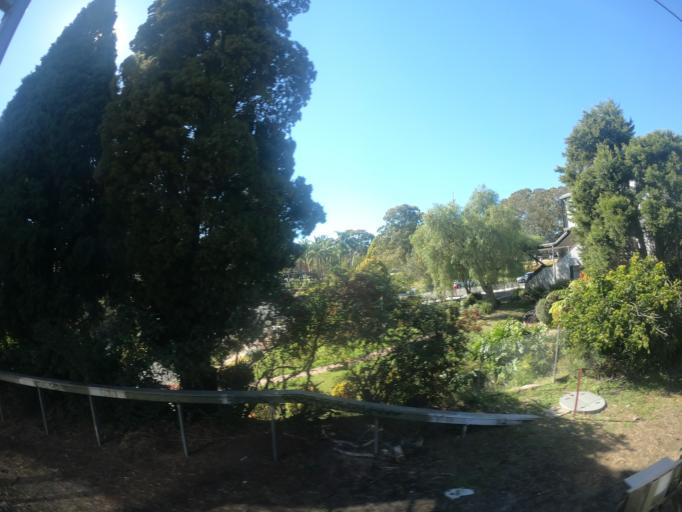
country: AU
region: New South Wales
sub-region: Hurstville
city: Oatley
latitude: -33.9805
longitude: 151.0797
